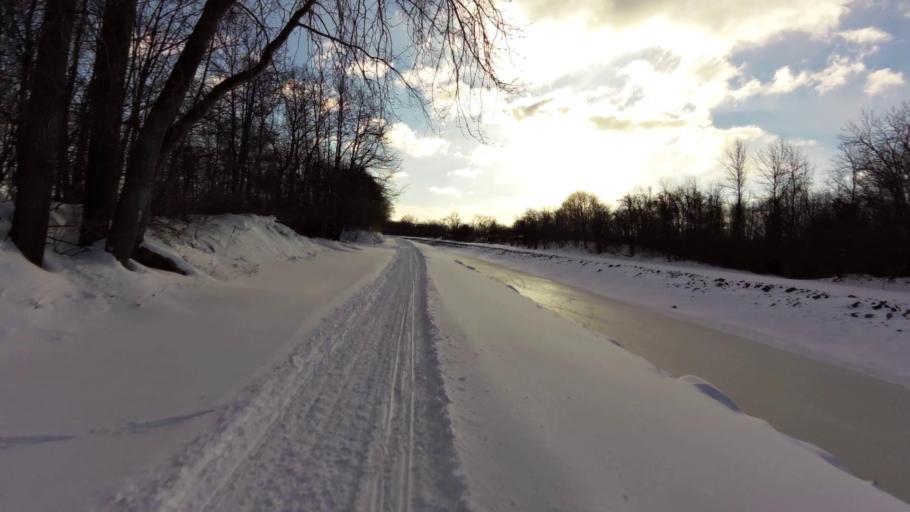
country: US
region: New York
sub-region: Orleans County
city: Albion
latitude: 43.2493
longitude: -78.1392
